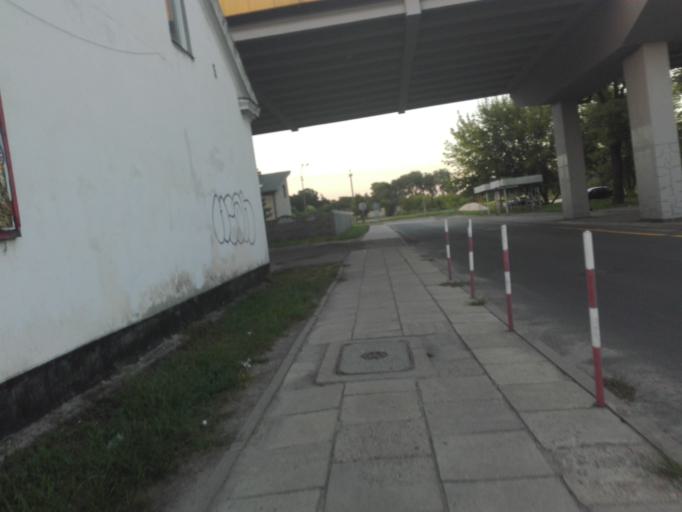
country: PL
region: Masovian Voivodeship
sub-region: Powiat sochaczewski
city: Sochaczew
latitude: 52.2172
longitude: 20.2413
